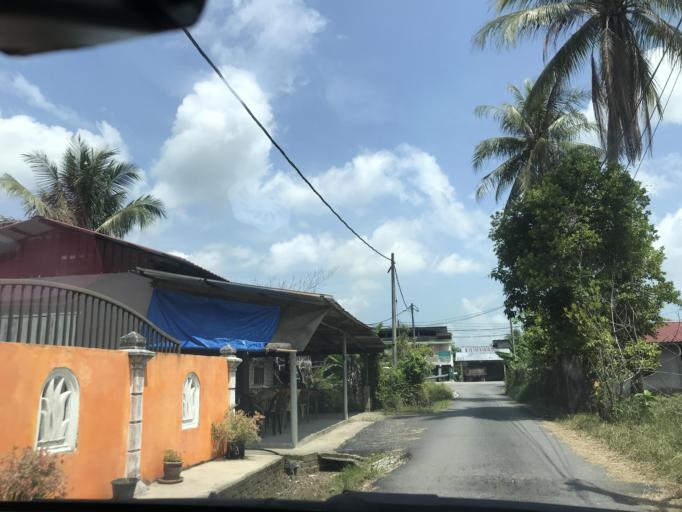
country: MY
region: Kelantan
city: Kota Bharu
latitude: 6.1142
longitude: 102.1778
